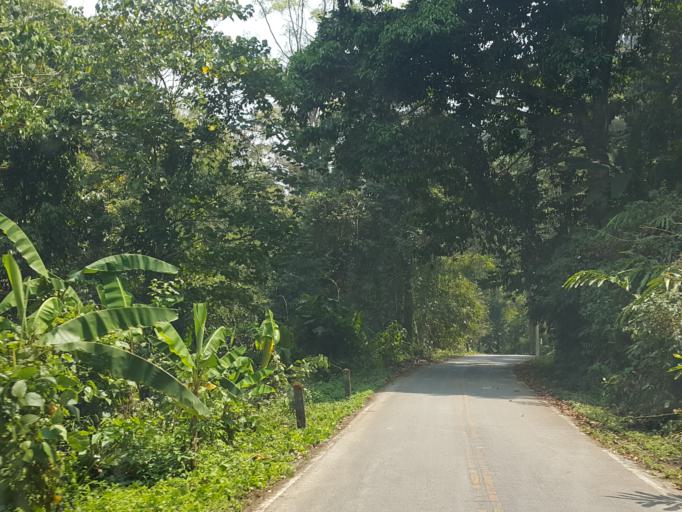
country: TH
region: Lampang
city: Mueang Pan
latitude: 18.8184
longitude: 99.4385
